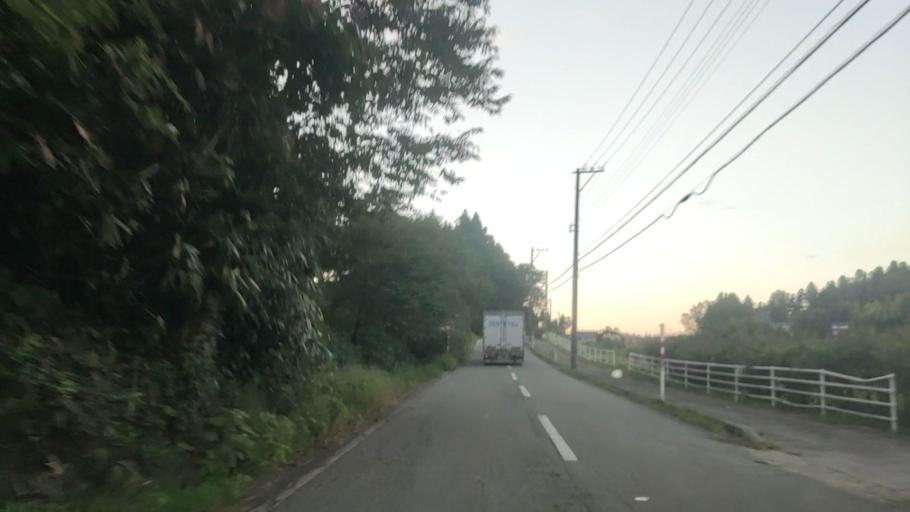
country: JP
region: Ishikawa
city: Tsubata
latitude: 36.6496
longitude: 136.7598
